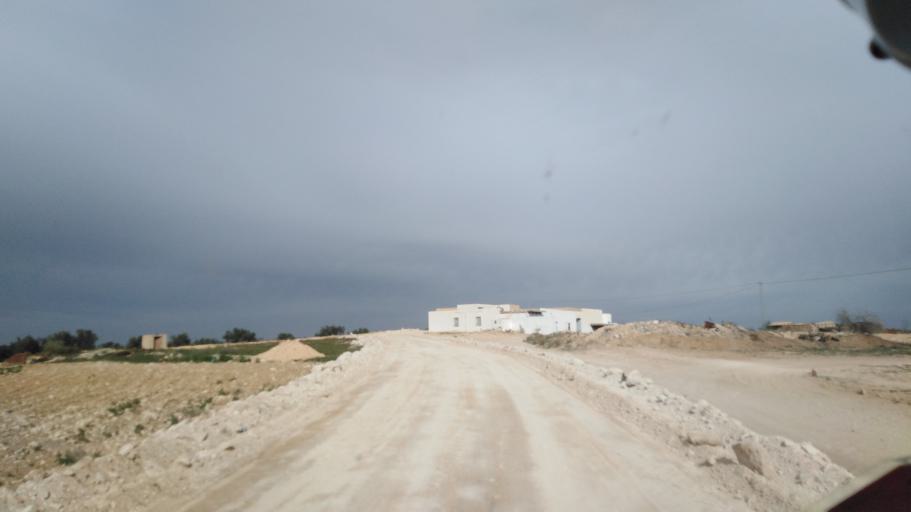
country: TN
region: Safaqis
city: Bi'r `Ali Bin Khalifah
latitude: 34.8145
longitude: 10.3075
